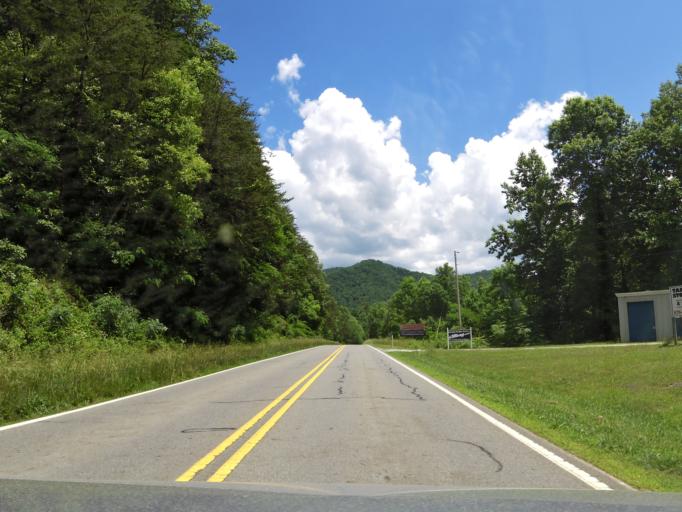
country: US
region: North Carolina
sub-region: Graham County
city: Robbinsville
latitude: 35.3573
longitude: -83.8368
